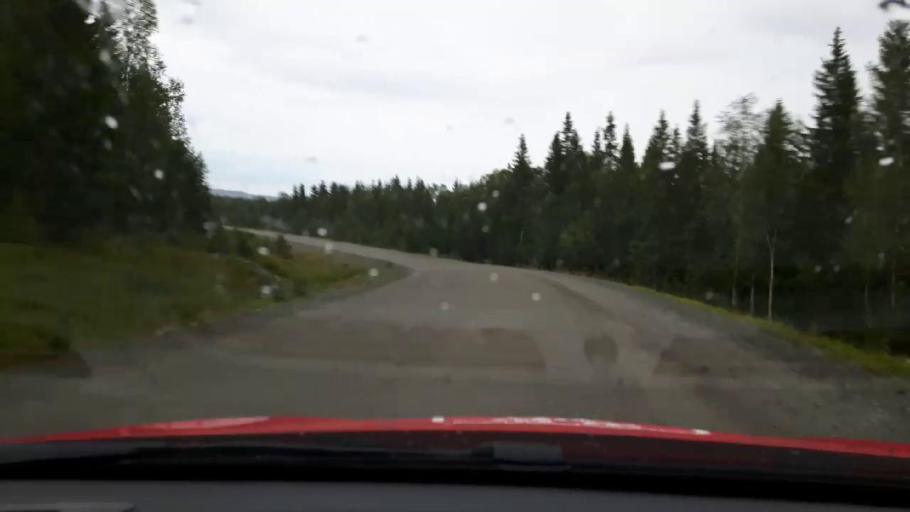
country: SE
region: Jaemtland
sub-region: Are Kommun
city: Are
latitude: 63.4489
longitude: 12.6633
